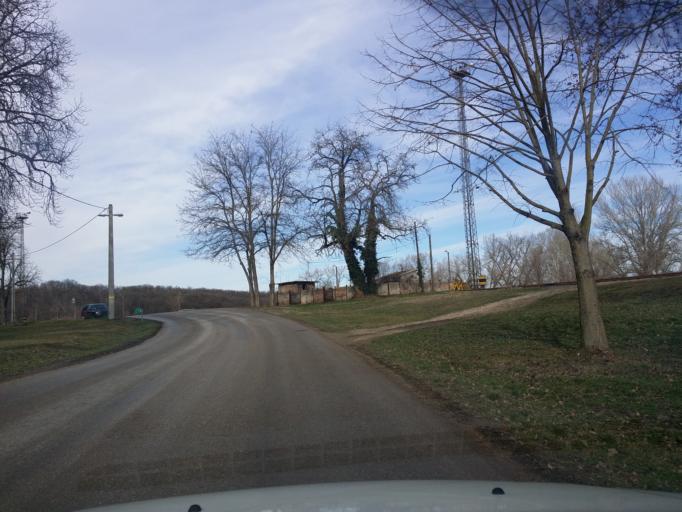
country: HU
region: Baranya
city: Villany
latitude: 45.8770
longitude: 18.4544
